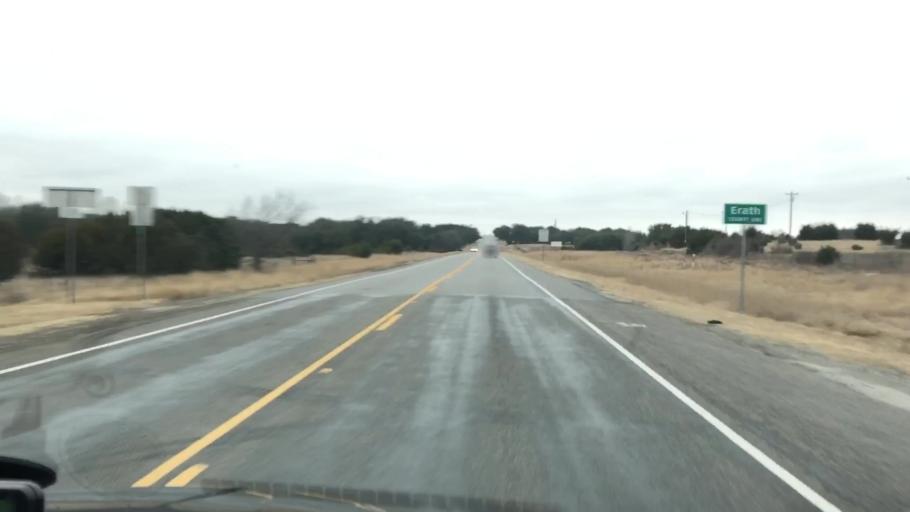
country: US
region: Texas
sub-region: Hamilton County
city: Hico
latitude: 31.9969
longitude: -98.0476
